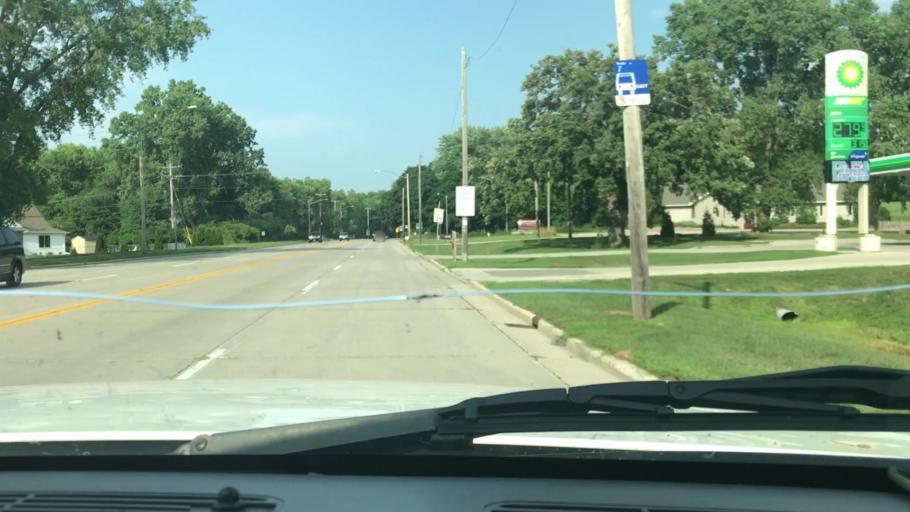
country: US
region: Wisconsin
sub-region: Brown County
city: Green Bay
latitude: 44.5290
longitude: -87.9383
